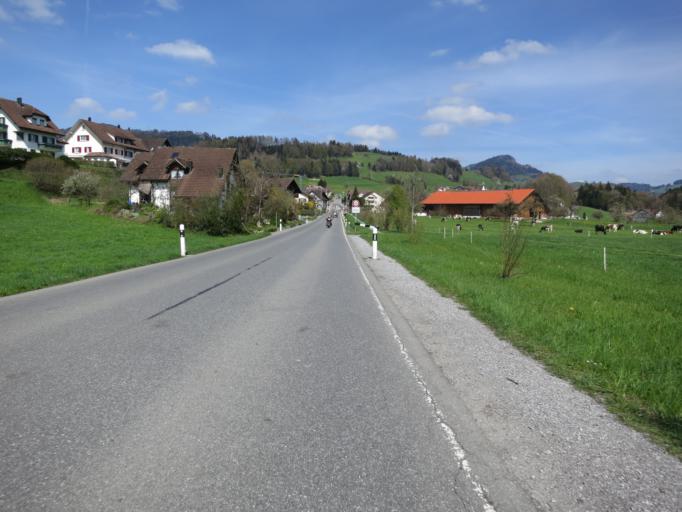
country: CH
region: Saint Gallen
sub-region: Wahlkreis See-Gaster
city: Eschenbach
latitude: 47.2469
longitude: 8.9420
